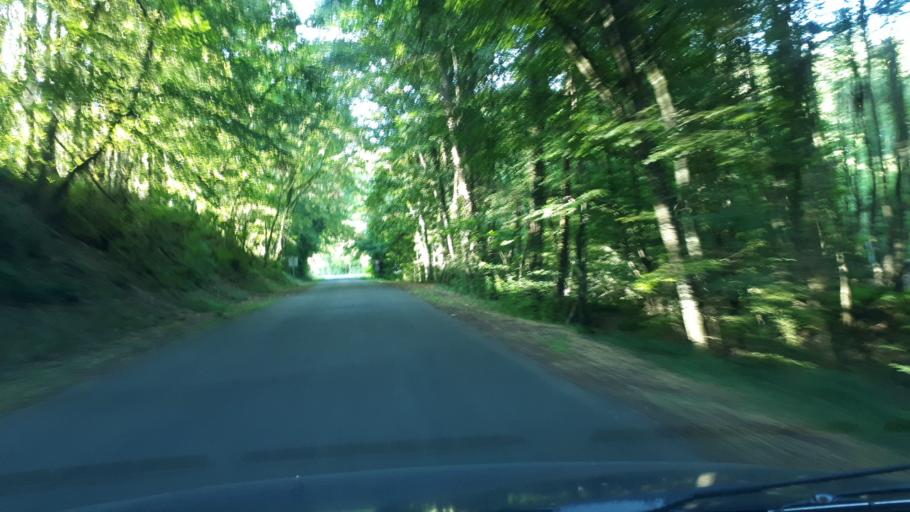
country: FR
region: Centre
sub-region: Departement du Loir-et-Cher
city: Villiers-sur-Loir
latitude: 47.7671
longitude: 0.9588
